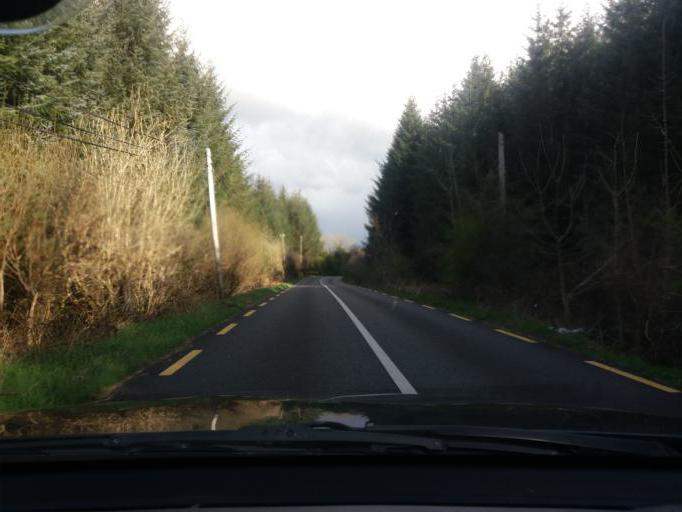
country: IE
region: Connaught
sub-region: County Leitrim
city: Manorhamilton
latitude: 54.3306
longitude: -8.2133
